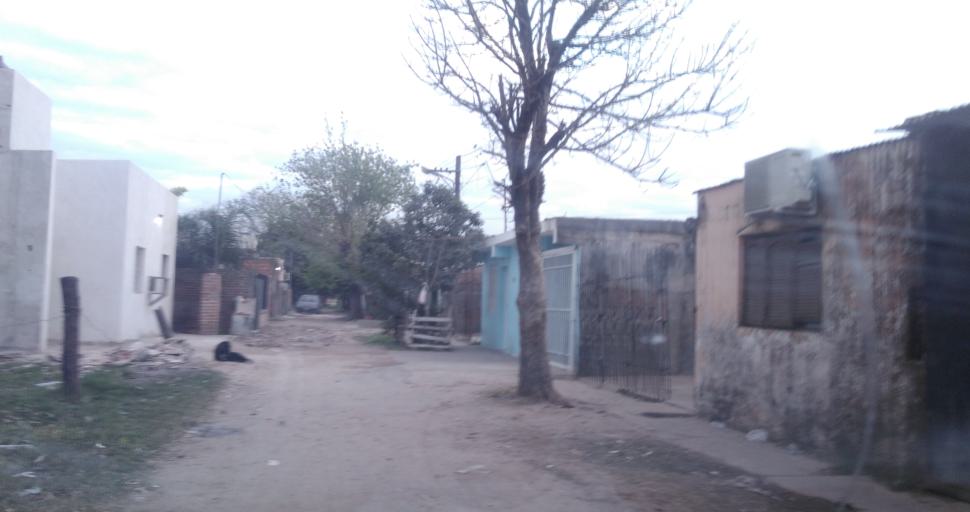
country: AR
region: Chaco
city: Fontana
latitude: -27.4485
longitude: -59.0373
